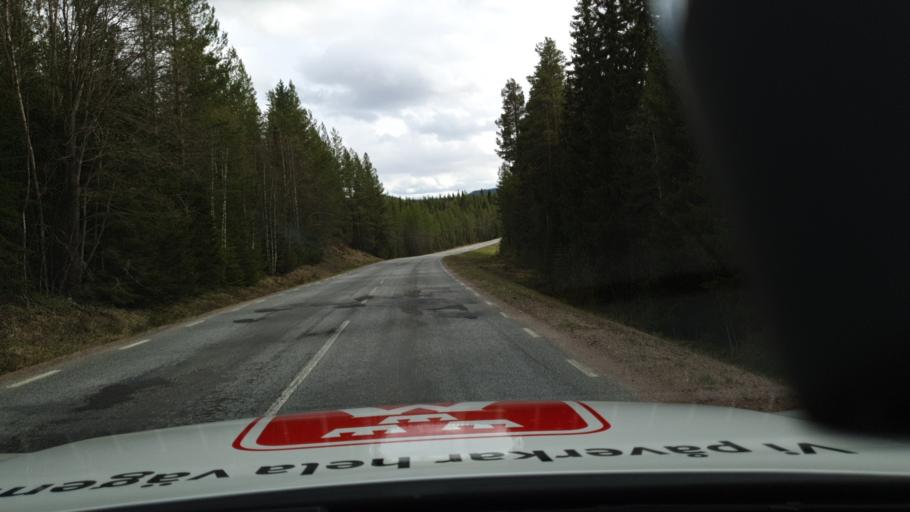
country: SE
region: Jaemtland
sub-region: Braecke Kommun
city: Braecke
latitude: 62.8435
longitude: 15.4755
